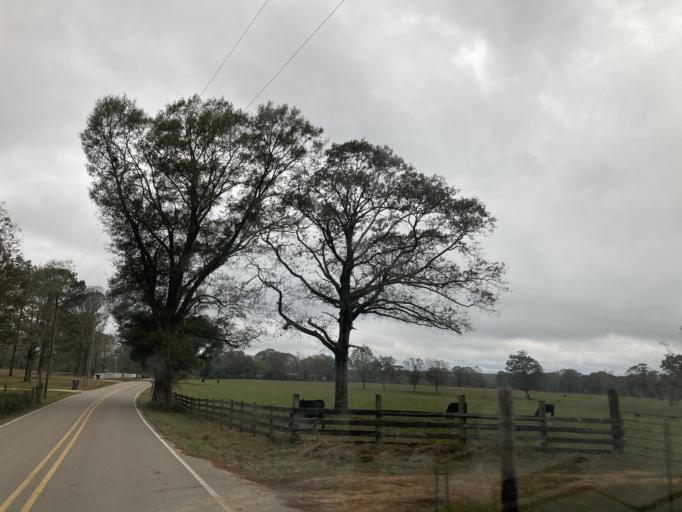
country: US
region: Mississippi
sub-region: Lamar County
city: Purvis
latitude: 31.1822
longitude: -89.4537
